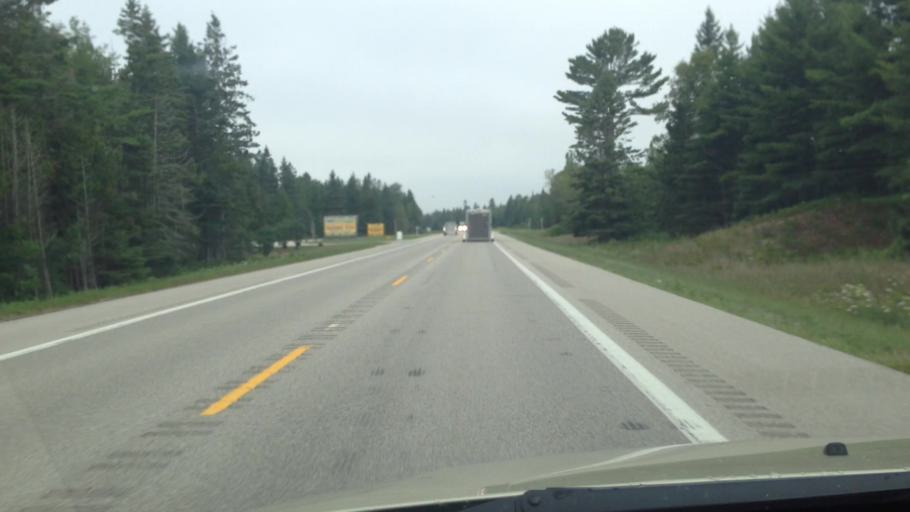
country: US
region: Michigan
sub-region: Luce County
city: Newberry
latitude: 46.0702
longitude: -85.2718
